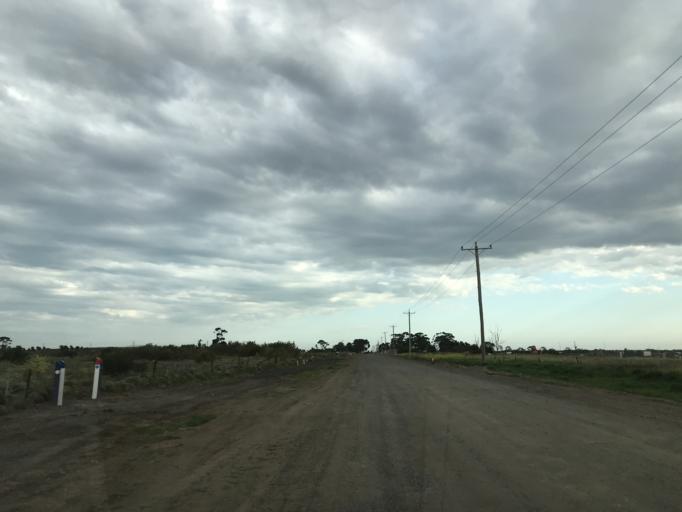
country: AU
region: Victoria
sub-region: Wyndham
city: Truganina
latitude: -37.8170
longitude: 144.7222
